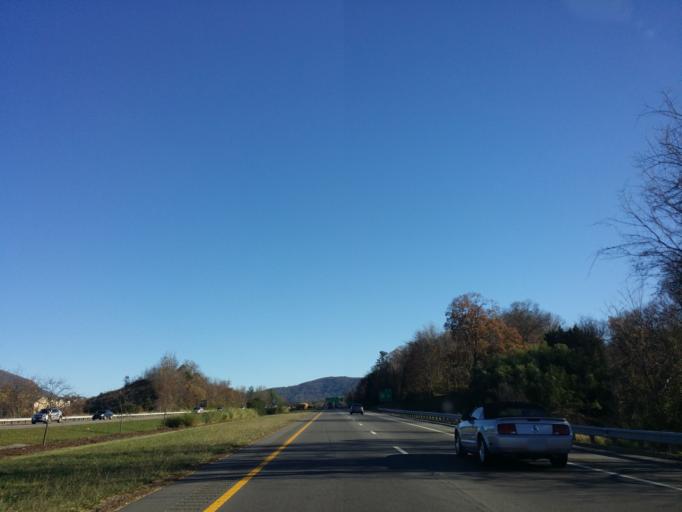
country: US
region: North Carolina
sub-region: Buncombe County
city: Biltmore Forest
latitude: 35.5747
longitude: -82.5161
